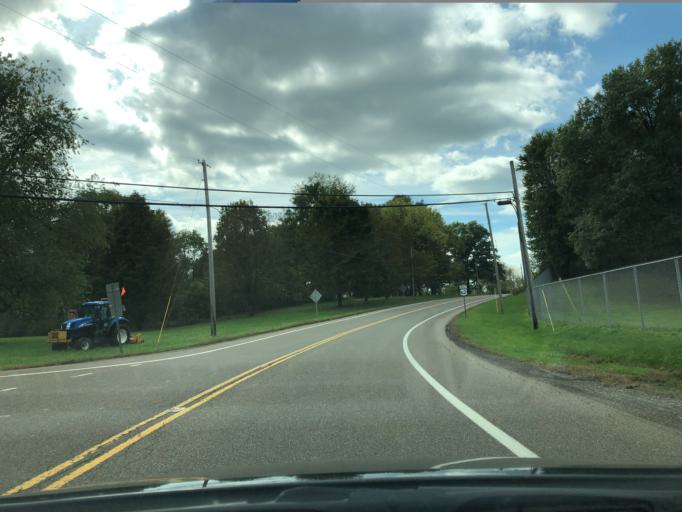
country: US
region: Ohio
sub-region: Stark County
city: Brewster
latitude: 40.6863
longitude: -81.5995
